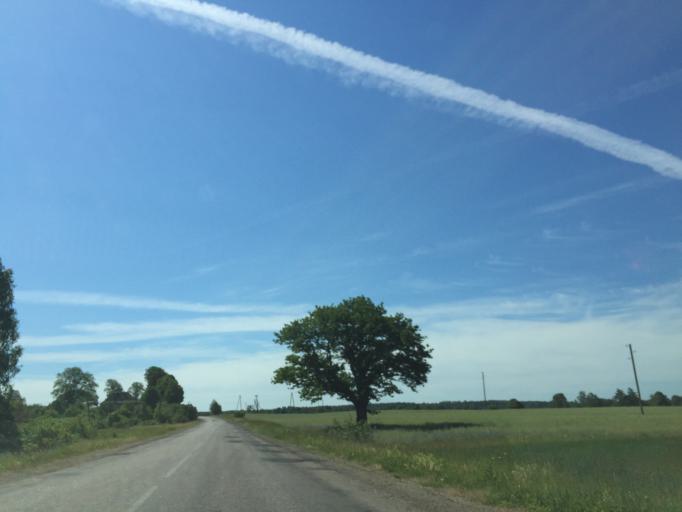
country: LV
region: Aizpute
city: Aizpute
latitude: 56.7183
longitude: 21.7592
